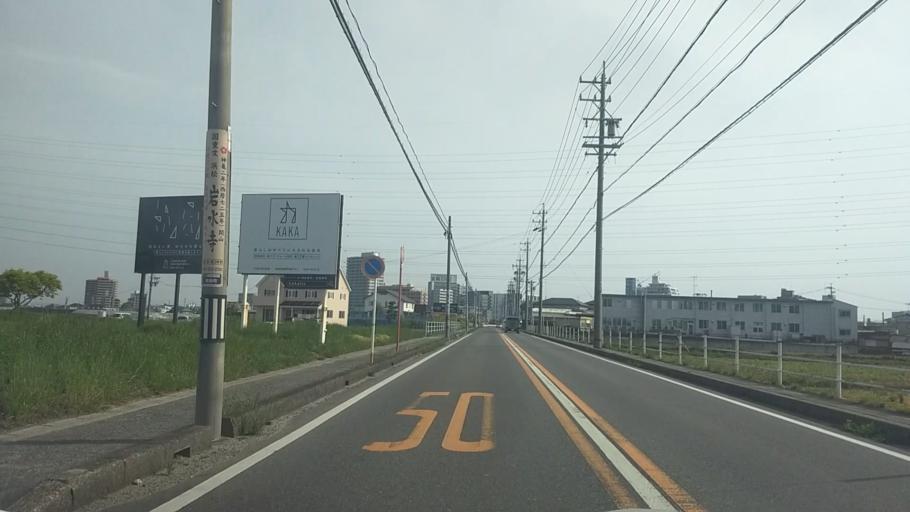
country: JP
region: Aichi
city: Anjo
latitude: 34.9598
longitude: 137.0580
